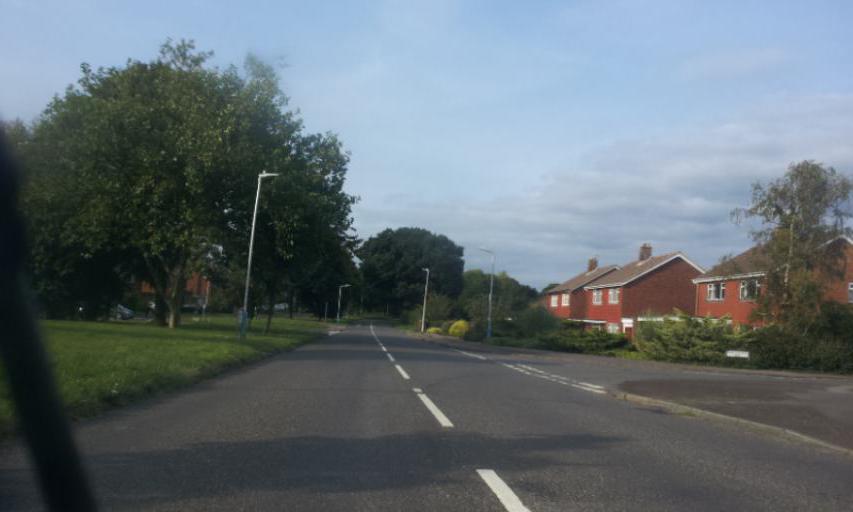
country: GB
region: England
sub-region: Kent
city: Tonbridge
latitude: 51.2137
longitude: 0.3003
